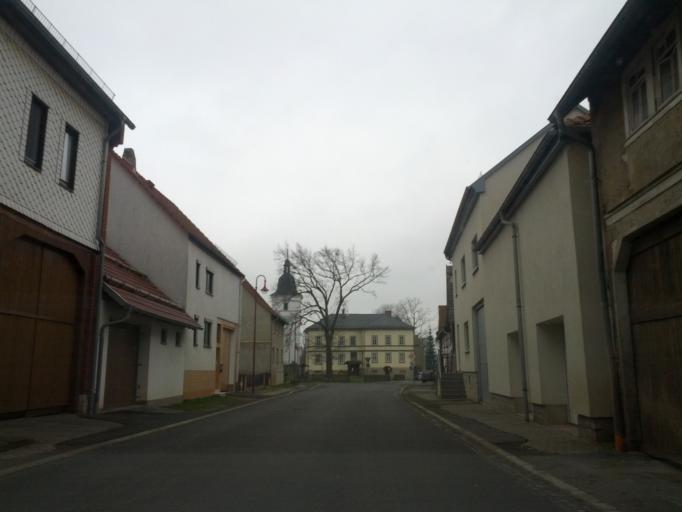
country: DE
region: Thuringia
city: Sonneborn
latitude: 51.0361
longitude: 10.5832
